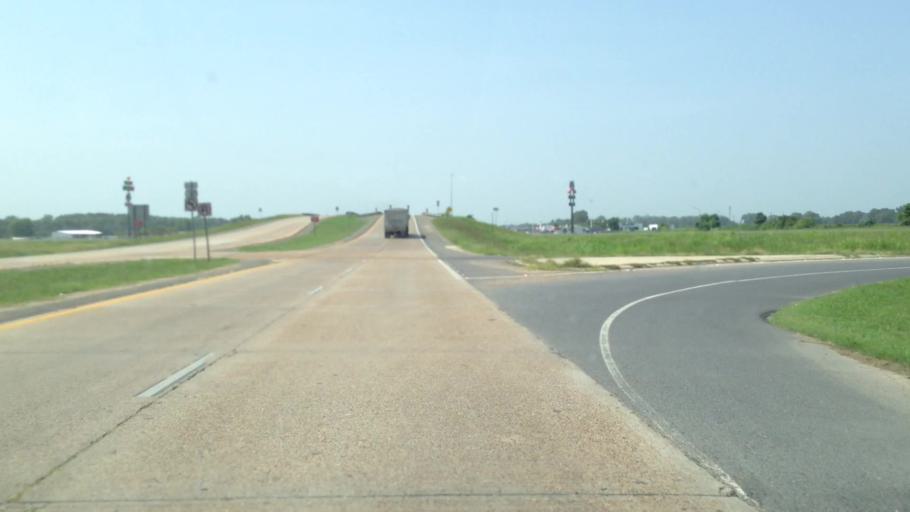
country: US
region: Louisiana
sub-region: Madison Parish
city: Tallulah
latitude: 32.3949
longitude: -91.1995
